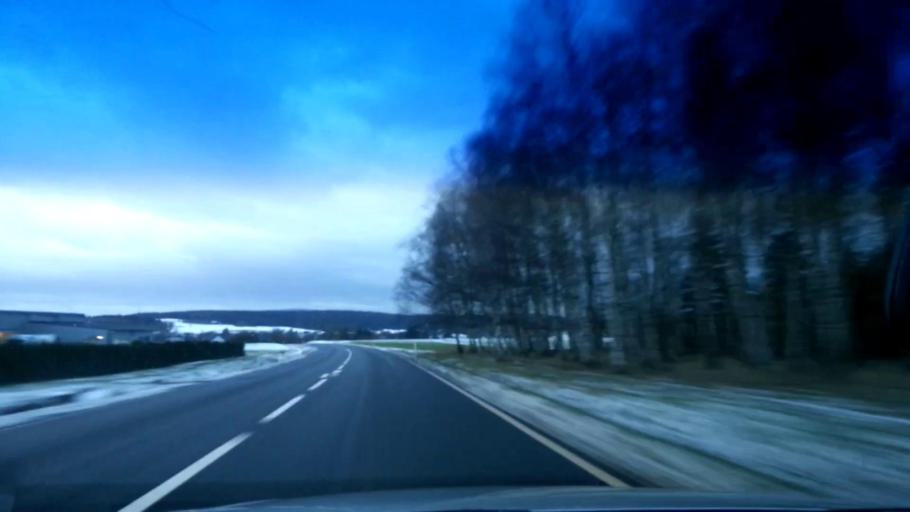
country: DE
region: Bavaria
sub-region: Upper Franconia
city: Marktleuthen
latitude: 50.1353
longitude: 12.0086
